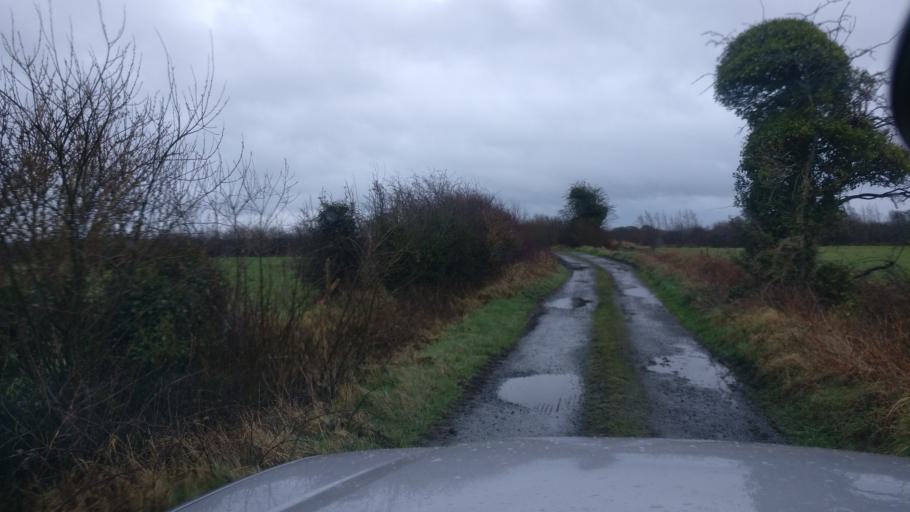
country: IE
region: Connaught
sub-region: County Galway
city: Ballinasloe
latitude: 53.2509
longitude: -8.3298
